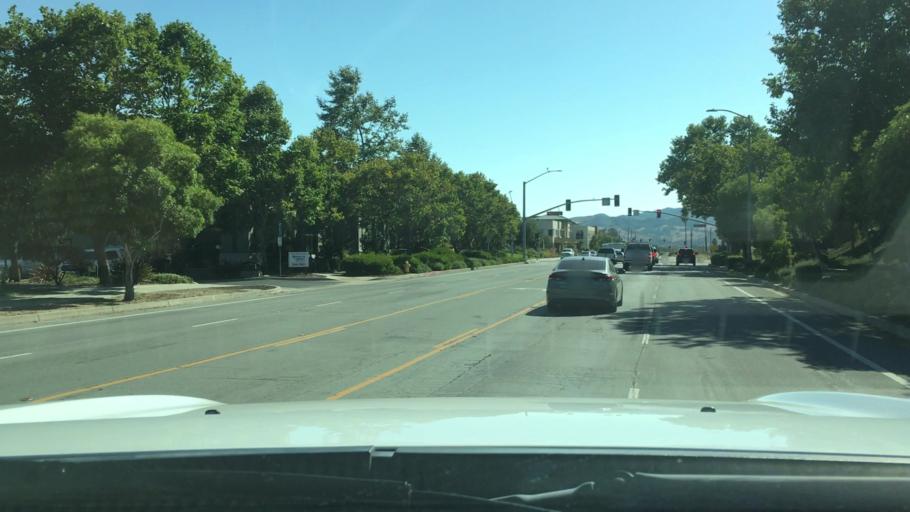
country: US
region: California
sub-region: San Luis Obispo County
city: San Luis Obispo
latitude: 35.2489
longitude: -120.6418
